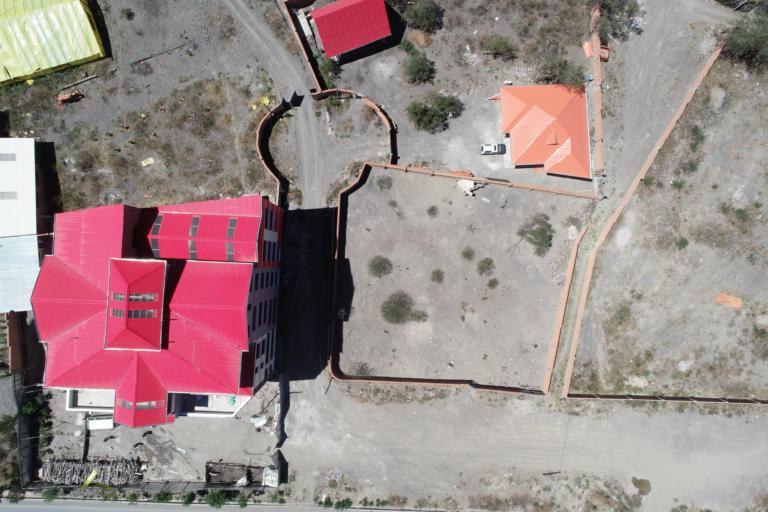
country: BO
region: La Paz
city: La Paz
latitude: -16.6262
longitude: -68.0526
